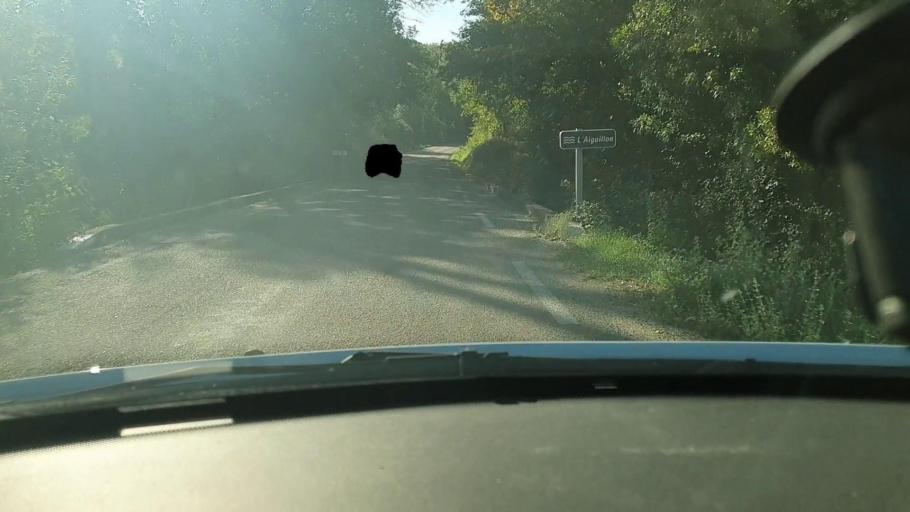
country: FR
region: Languedoc-Roussillon
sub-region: Departement du Gard
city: Goudargues
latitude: 44.1921
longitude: 4.4812
